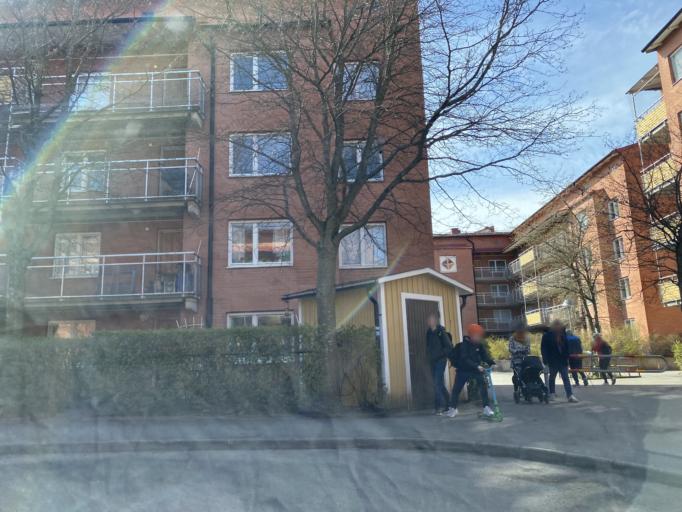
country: SE
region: Stockholm
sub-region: Stockholms Kommun
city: Arsta
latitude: 59.2805
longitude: 18.0088
